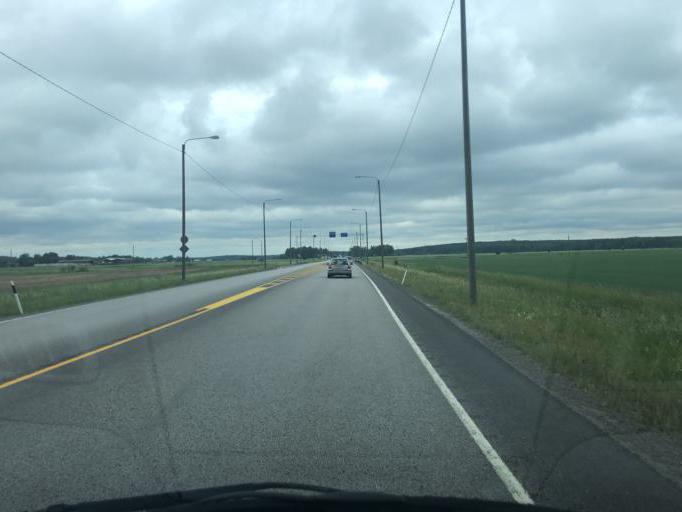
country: FI
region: Uusimaa
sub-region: Loviisa
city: Lapinjaervi
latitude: 60.6537
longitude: 26.2391
